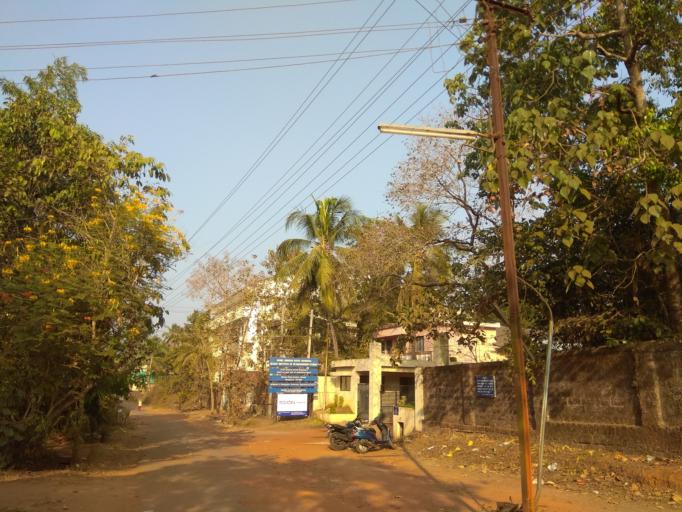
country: IN
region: Karnataka
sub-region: Dakshina Kannada
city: Mangalore
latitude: 12.9249
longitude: 74.8696
